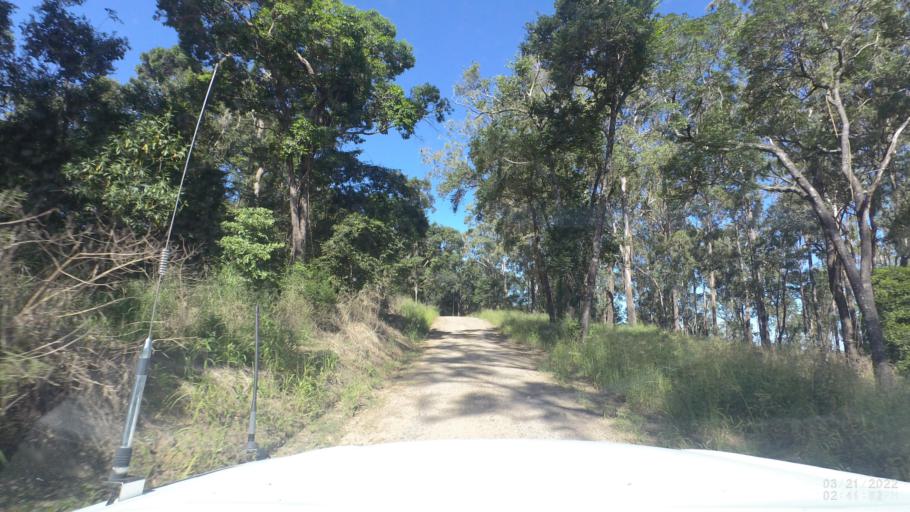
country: AU
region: Queensland
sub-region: Ipswich
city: Deebing Heights
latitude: -27.8296
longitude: 152.8232
